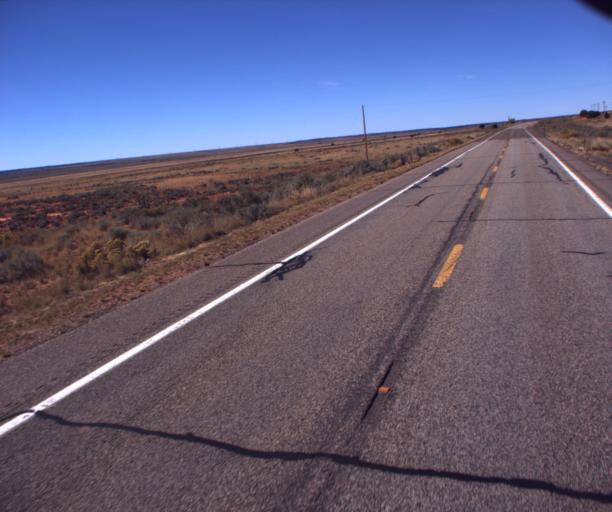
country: US
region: Arizona
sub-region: Mohave County
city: Colorado City
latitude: 36.8584
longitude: -112.8006
